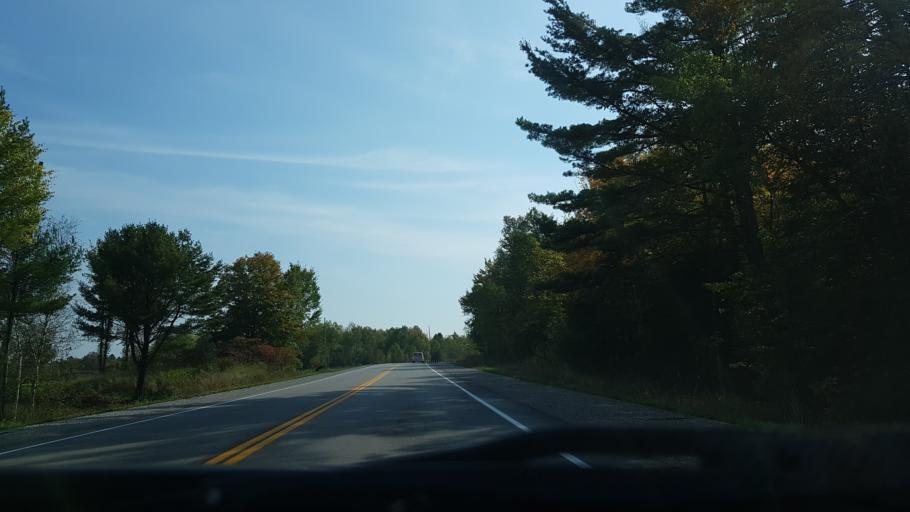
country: CA
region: Ontario
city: Orillia
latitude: 44.7407
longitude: -79.2983
